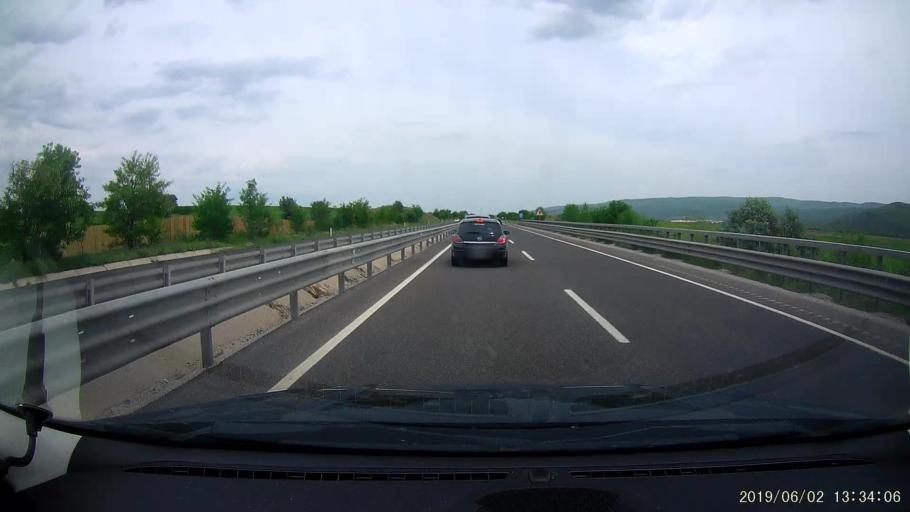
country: TR
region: Cankiri
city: Atkaracalar
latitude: 40.8026
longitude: 33.0231
